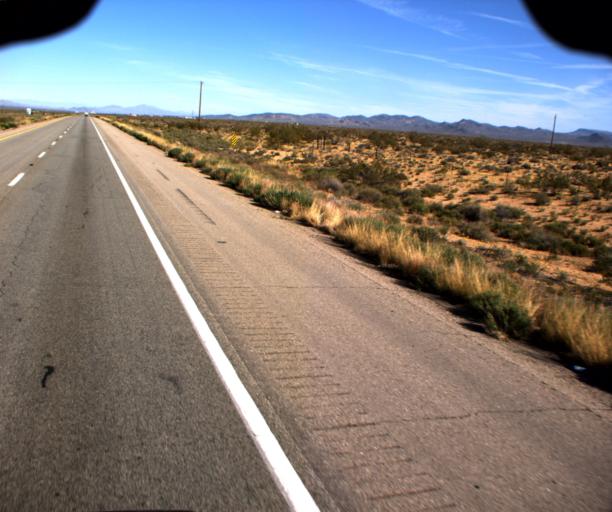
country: US
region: Arizona
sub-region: Mohave County
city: Dolan Springs
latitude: 35.5014
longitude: -114.3327
